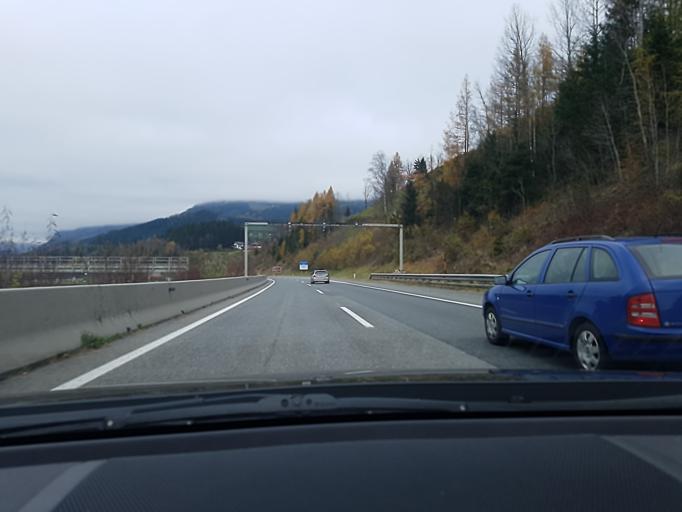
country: AT
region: Salzburg
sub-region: Politischer Bezirk Sankt Johann im Pongau
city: Pfarrwerfen
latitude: 47.4482
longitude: 13.2182
